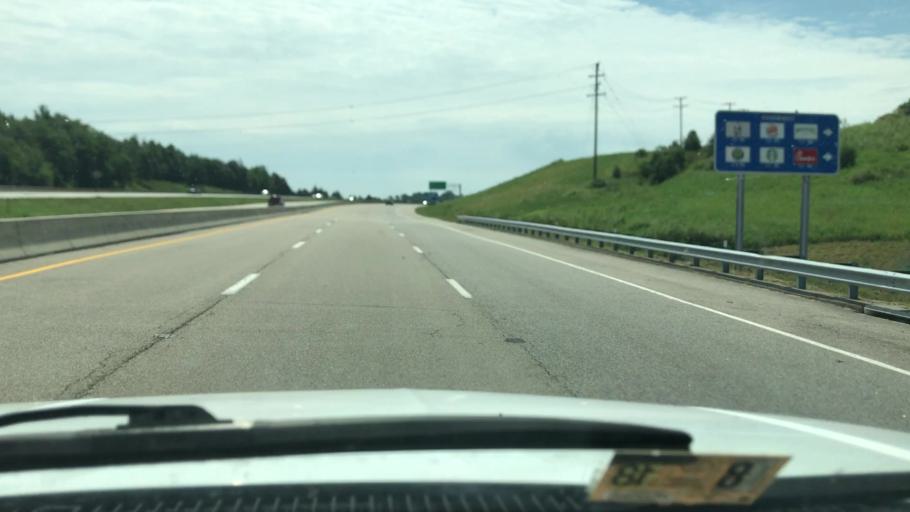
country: US
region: Virginia
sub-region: Chesterfield County
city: Brandermill
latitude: 37.5183
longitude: -77.6900
